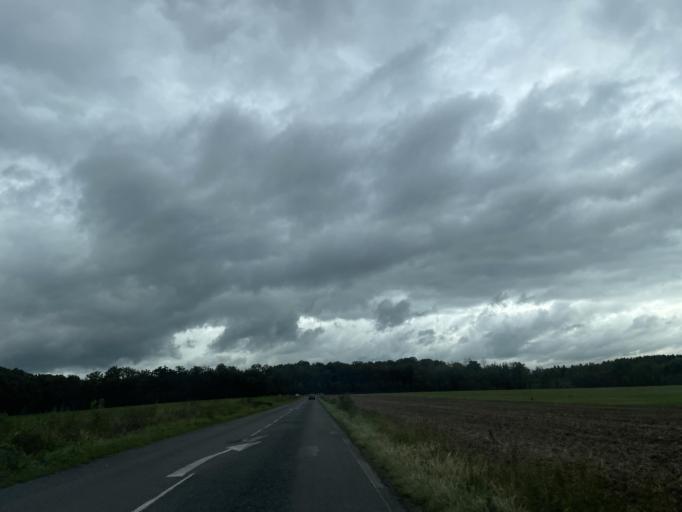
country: FR
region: Ile-de-France
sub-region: Departement de Seine-et-Marne
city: Sammeron
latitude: 48.8895
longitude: 3.0667
